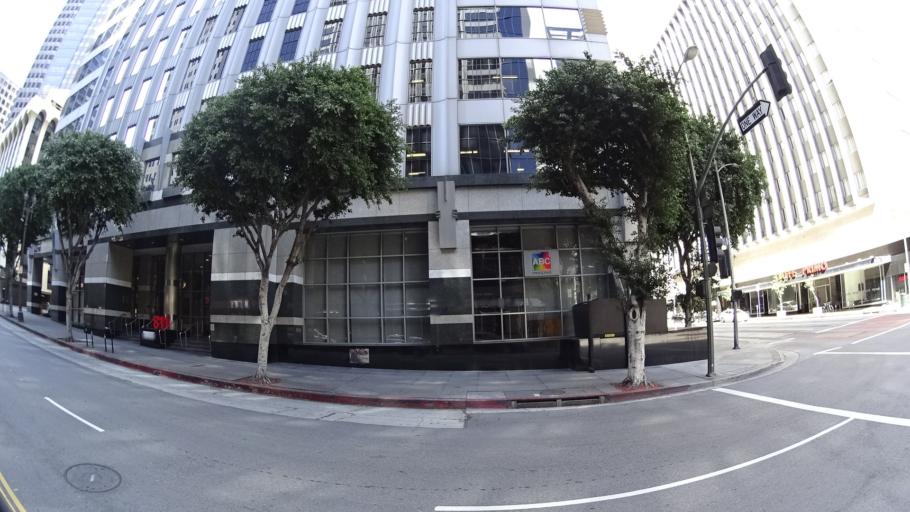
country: US
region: California
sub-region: Los Angeles County
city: Los Angeles
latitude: 34.0496
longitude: -118.2587
